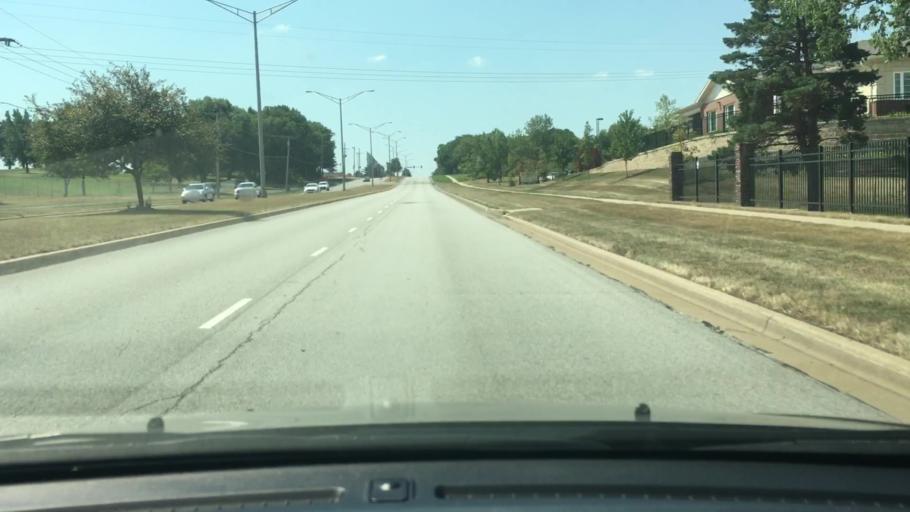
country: US
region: Kansas
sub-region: Johnson County
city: Lenexa
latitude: 38.9056
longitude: -94.7238
